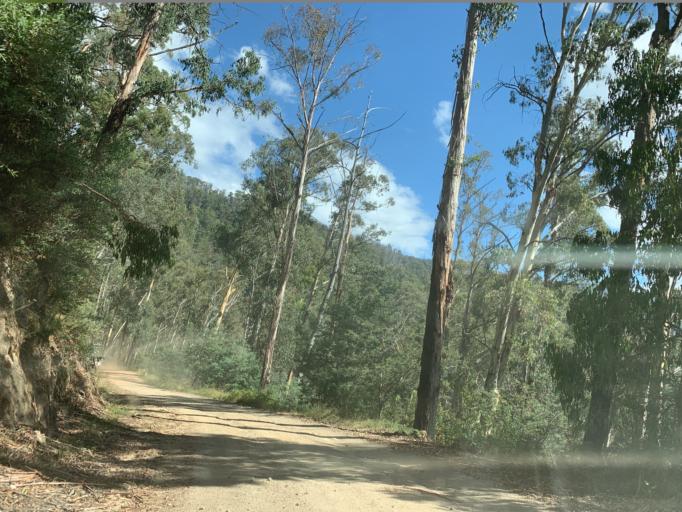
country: AU
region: Victoria
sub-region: Mansfield
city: Mansfield
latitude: -37.0911
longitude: 146.5266
